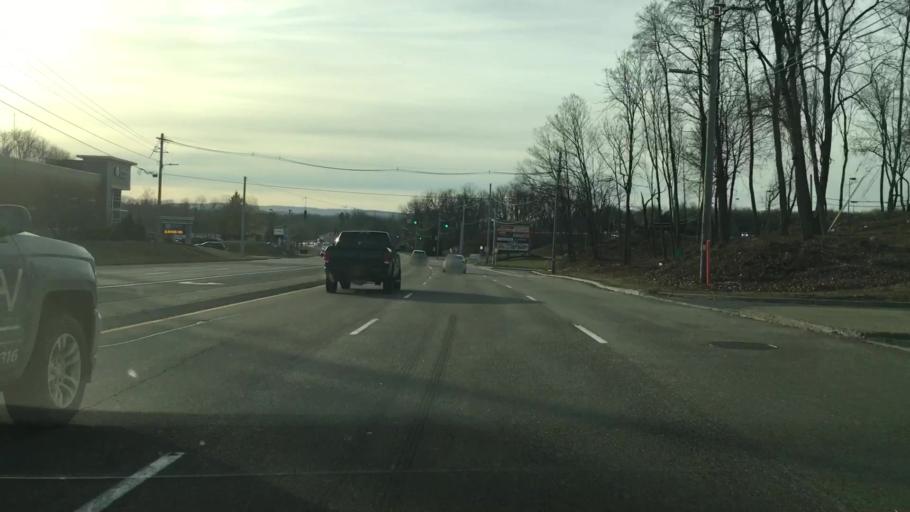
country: US
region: New York
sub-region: Dutchess County
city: Wappingers Falls
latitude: 41.6205
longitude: -73.9173
